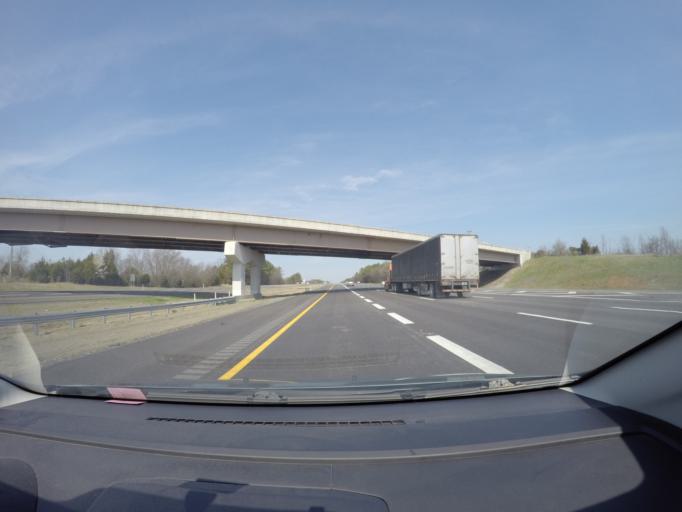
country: US
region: Tennessee
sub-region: Rutherford County
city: Murfreesboro
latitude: 35.8890
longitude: -86.4808
